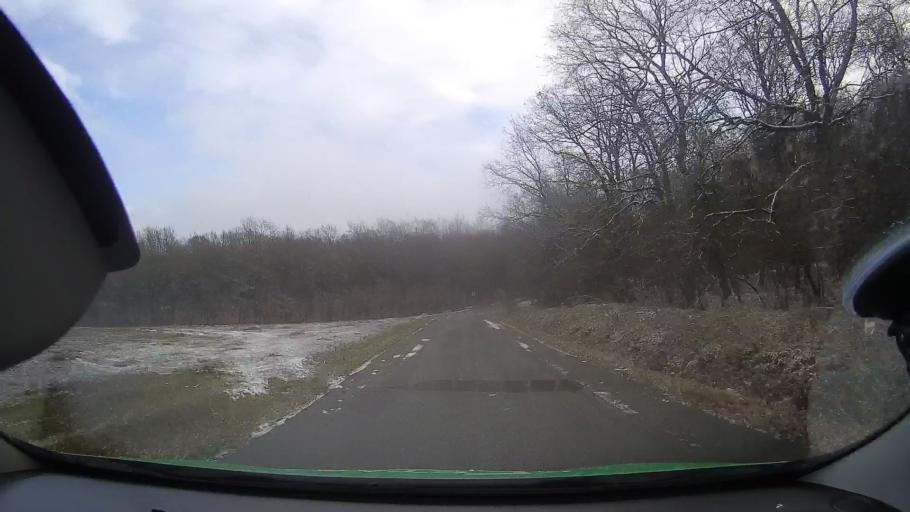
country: RO
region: Mures
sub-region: Comuna Ludus
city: Gheja
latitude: 46.4012
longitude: 24.0167
